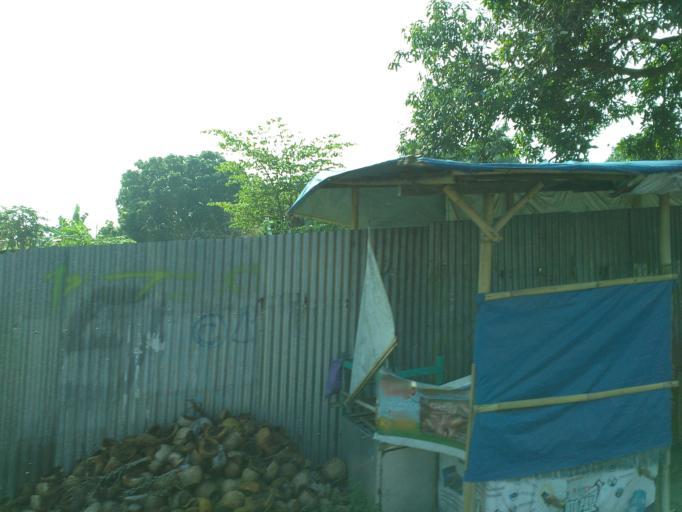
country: ID
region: Central Java
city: Delanggu
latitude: -7.6277
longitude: 110.6956
